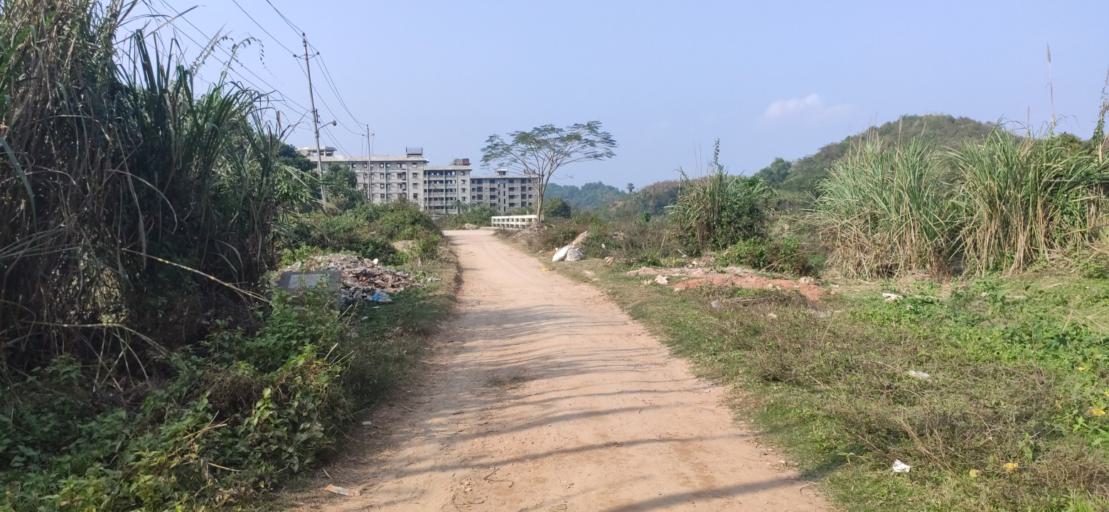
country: BD
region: Chittagong
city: Chittagong
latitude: 22.4748
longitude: 91.7845
